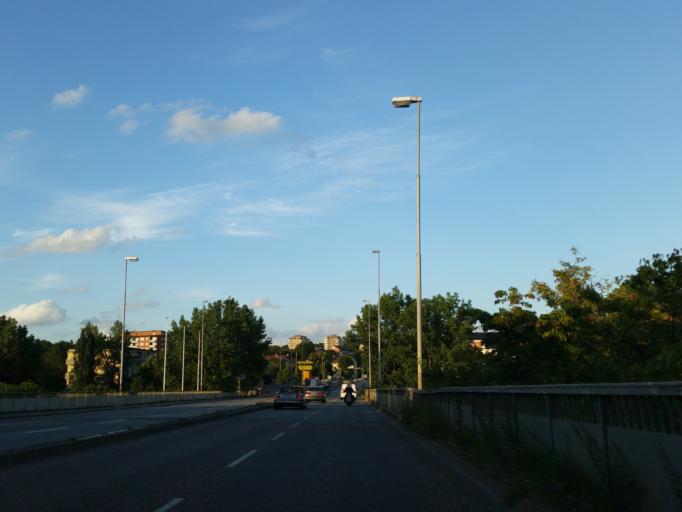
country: SE
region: Stockholm
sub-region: Sodertalje Kommun
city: Soedertaelje
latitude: 59.1986
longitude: 17.6238
